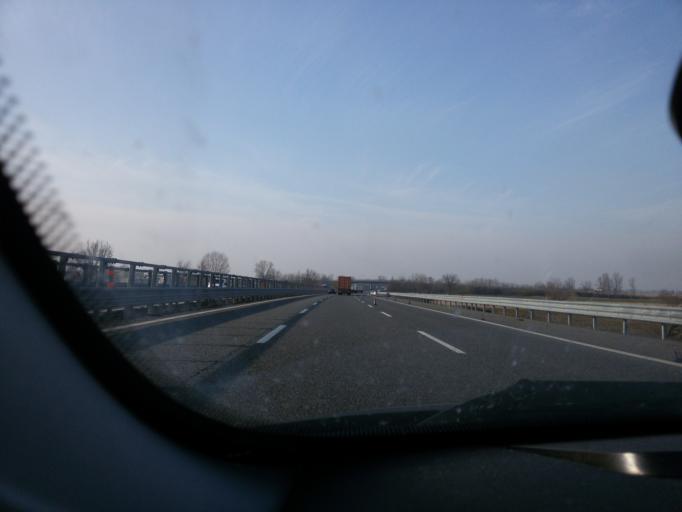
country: IT
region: Piedmont
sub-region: Provincia di Alessandria
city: Occimiano
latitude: 45.0539
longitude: 8.5181
